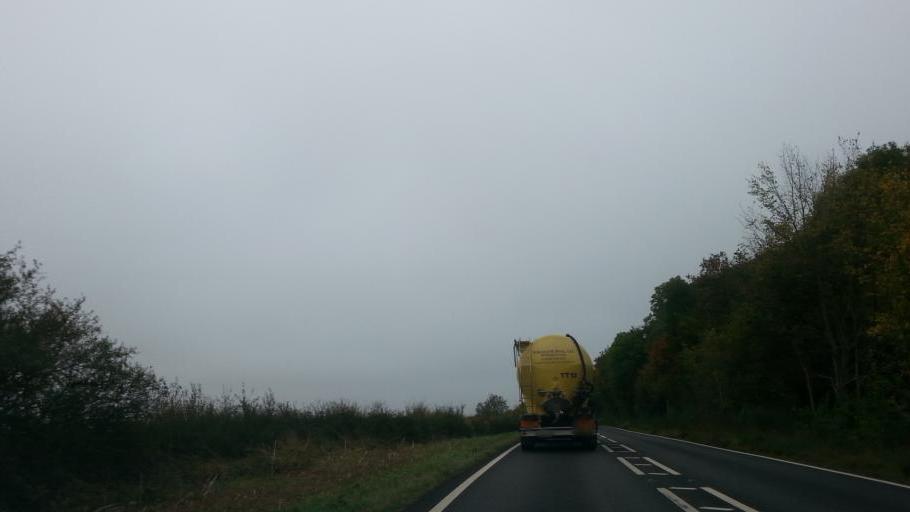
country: GB
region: England
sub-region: Northamptonshire
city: Oundle
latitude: 52.4467
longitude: -0.4663
